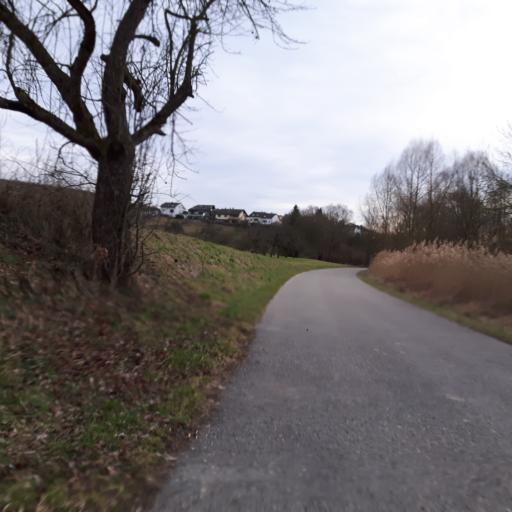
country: DE
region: Baden-Wuerttemberg
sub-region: Regierungsbezirk Stuttgart
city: Grossbottwar
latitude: 48.9871
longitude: 9.2915
